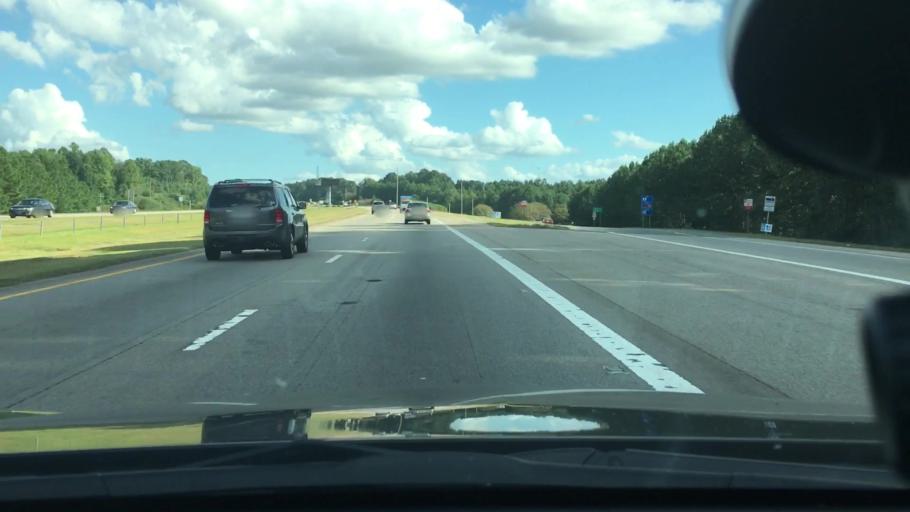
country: US
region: North Carolina
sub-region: Wake County
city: Cary
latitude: 35.8092
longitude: -78.7267
